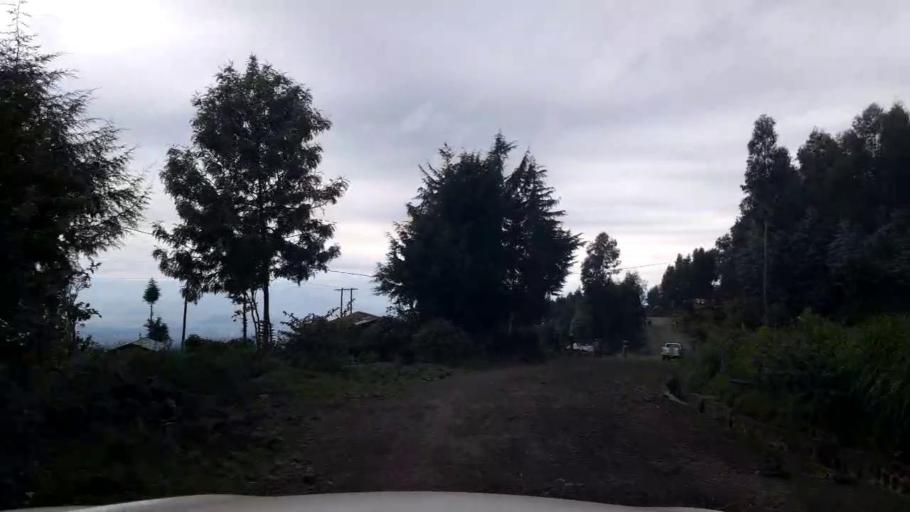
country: RW
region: Northern Province
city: Musanze
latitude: -1.4877
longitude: 29.5283
